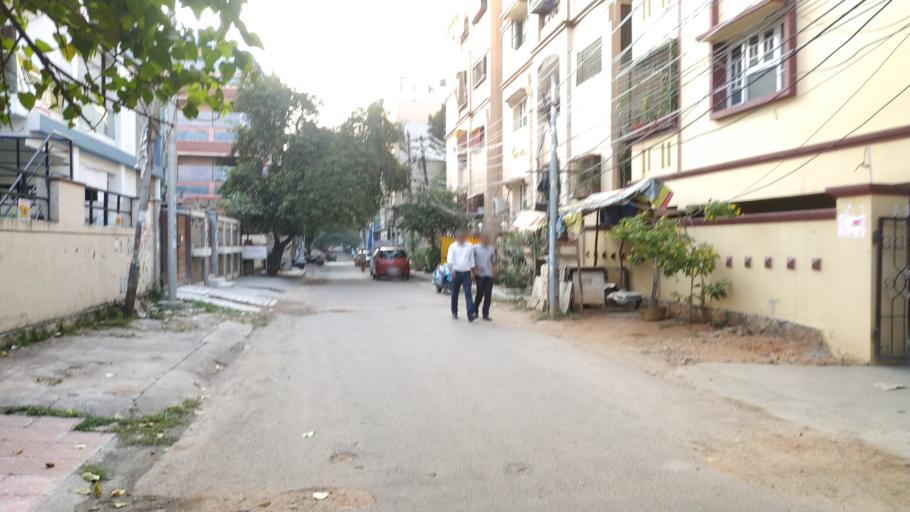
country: IN
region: Telangana
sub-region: Rangareddi
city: Kukatpalli
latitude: 17.4431
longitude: 78.4479
